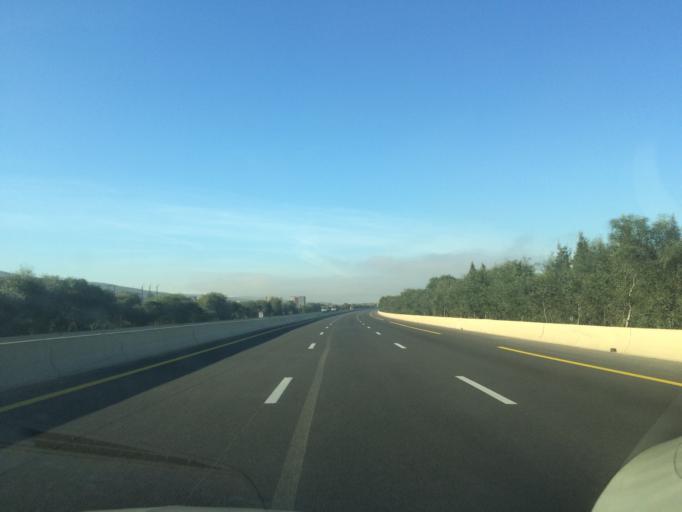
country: DZ
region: Relizane
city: Oued Rhiou
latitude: 36.0041
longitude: 1.0075
